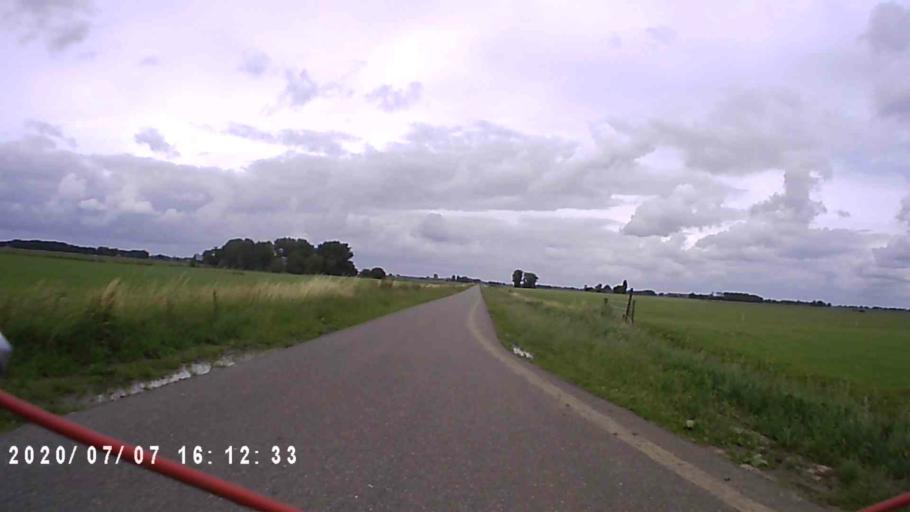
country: NL
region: Groningen
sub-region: Gemeente Winsum
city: Winsum
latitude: 53.3697
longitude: 6.5313
